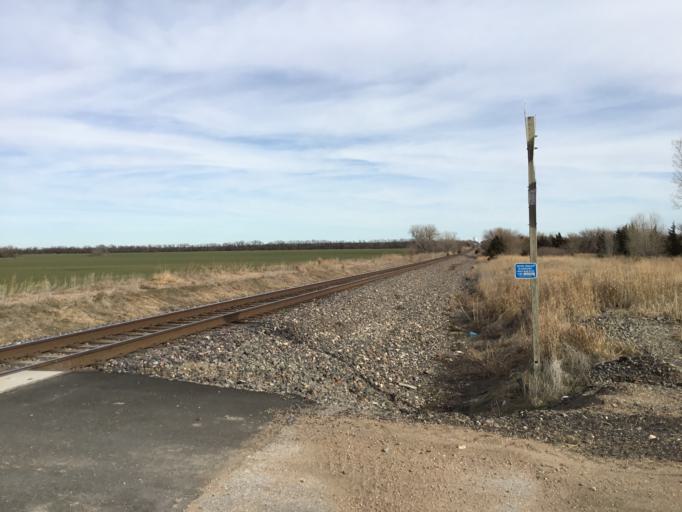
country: US
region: Kansas
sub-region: McPherson County
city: McPherson
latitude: 38.3843
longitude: -97.5931
